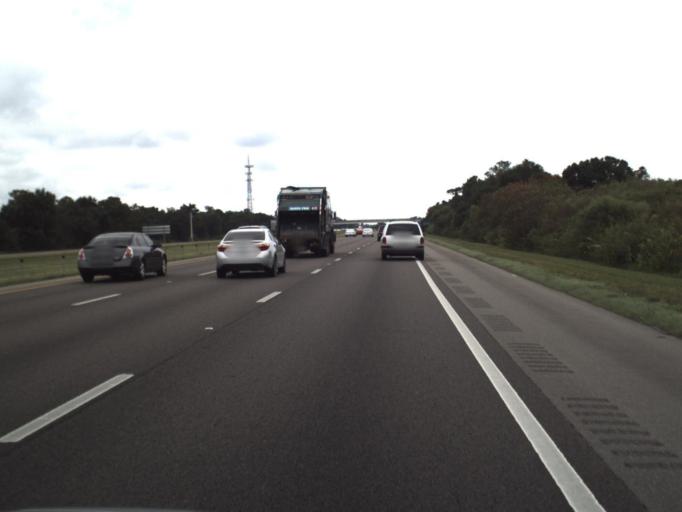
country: US
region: Florida
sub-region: Sarasota County
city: Desoto Lakes
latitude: 27.4239
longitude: -82.4588
